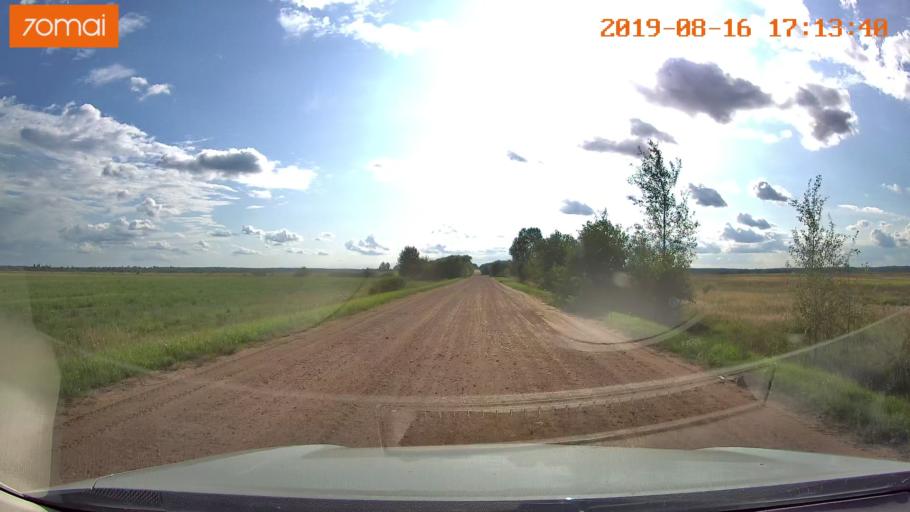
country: BY
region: Mogilev
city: Hlusha
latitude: 53.1883
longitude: 28.8717
